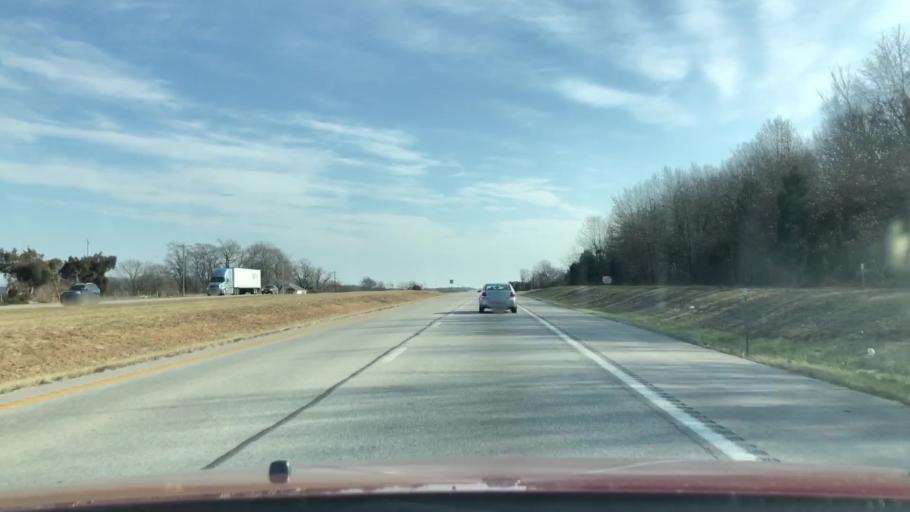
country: US
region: Missouri
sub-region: Christian County
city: Ozark
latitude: 37.1196
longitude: -93.1675
